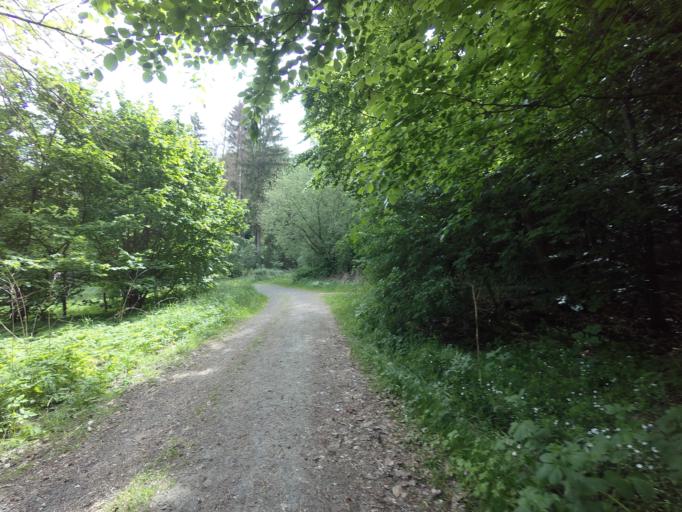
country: DE
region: Lower Saxony
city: Erkerode
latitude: 52.2053
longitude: 10.7385
